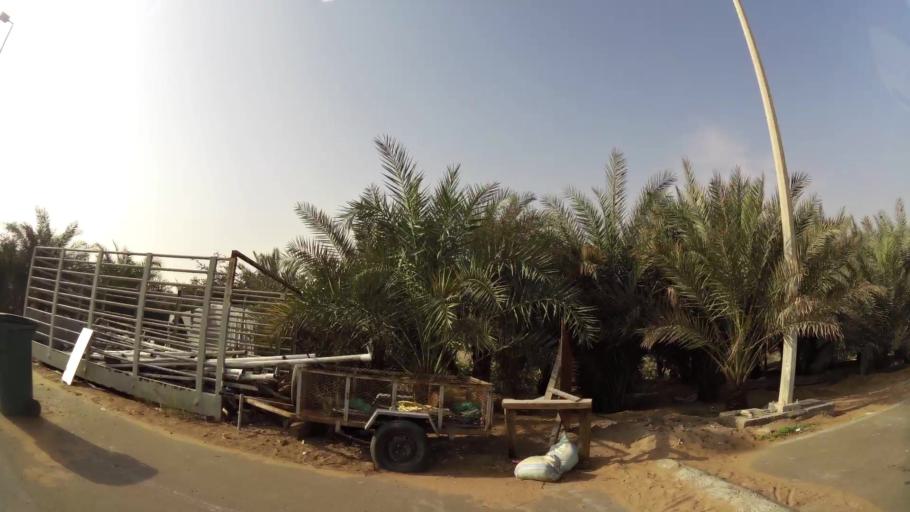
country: AE
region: Abu Dhabi
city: Abu Dhabi
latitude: 24.2674
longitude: 54.6614
